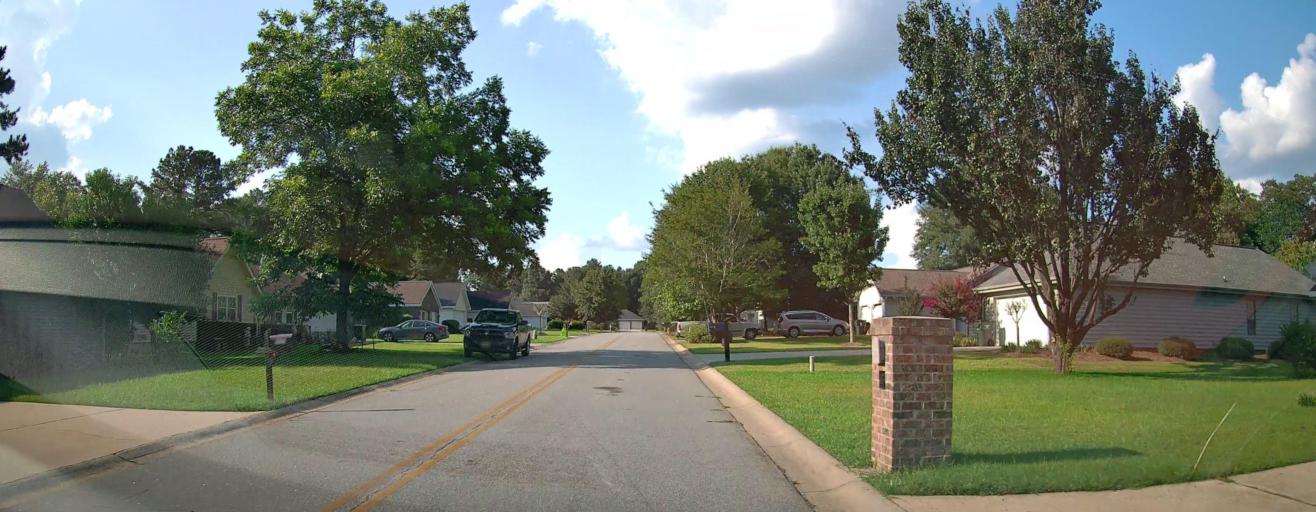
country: US
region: Georgia
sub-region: Houston County
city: Warner Robins
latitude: 32.5878
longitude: -83.6413
